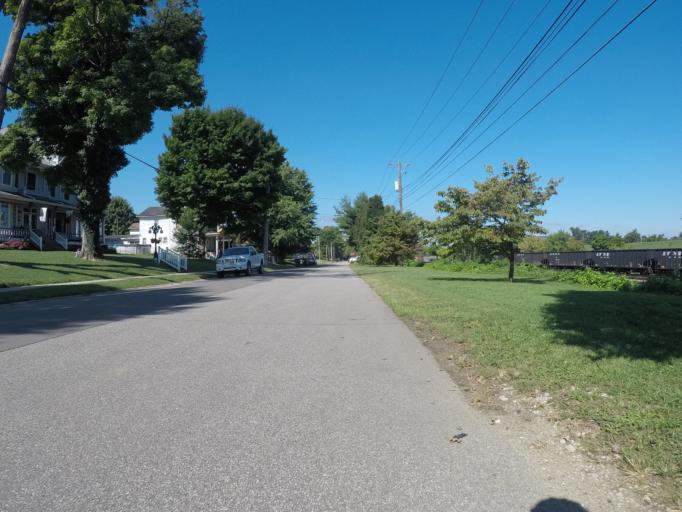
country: US
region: West Virginia
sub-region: Wayne County
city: Ceredo
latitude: 38.3999
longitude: -82.5664
